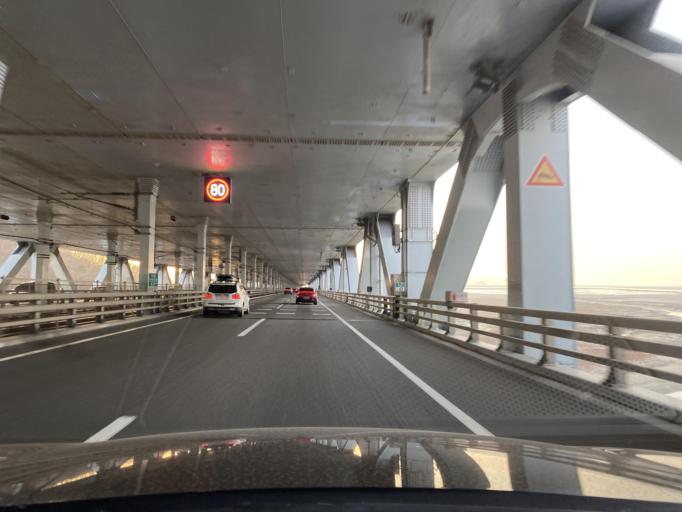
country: KR
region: Gyeonggi-do
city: Tongjin
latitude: 37.5432
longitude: 126.5761
